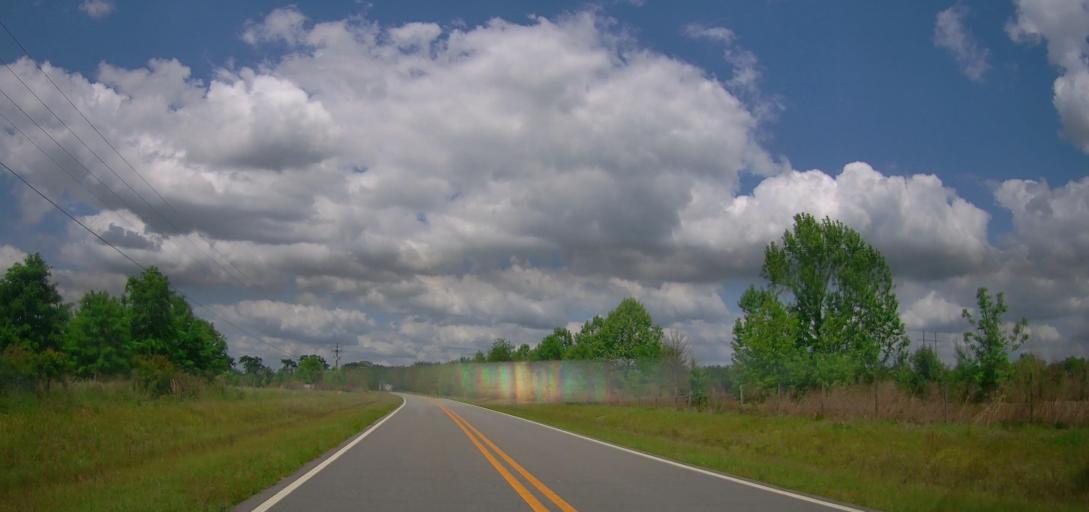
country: US
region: Georgia
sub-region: Laurens County
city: Dublin
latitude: 32.5963
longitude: -82.9305
